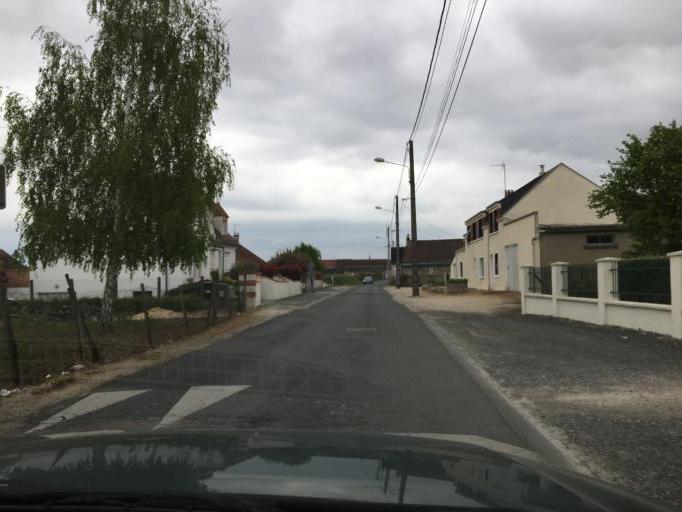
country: FR
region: Centre
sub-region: Departement du Loiret
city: Saint-Jean-de-la-Ruelle
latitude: 47.9210
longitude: 1.8711
